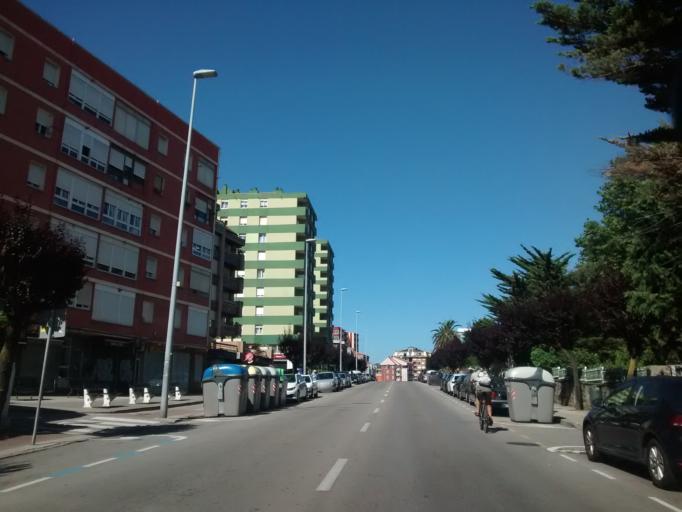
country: ES
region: Cantabria
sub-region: Provincia de Cantabria
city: Santander
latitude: 43.4656
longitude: -3.8173
